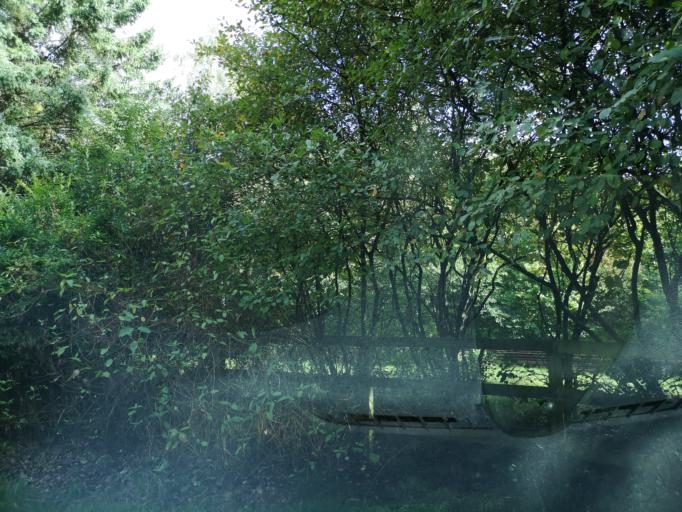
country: DK
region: Central Jutland
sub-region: Ringkobing-Skjern Kommune
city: Skjern
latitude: 55.9421
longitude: 8.5293
